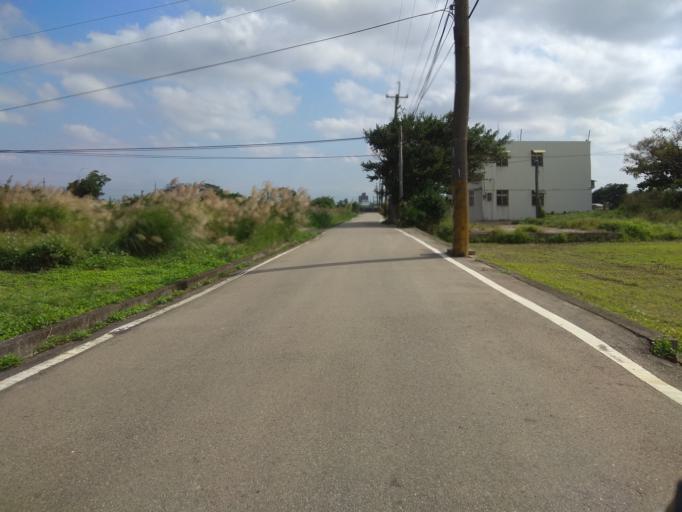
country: TW
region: Taiwan
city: Taoyuan City
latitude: 25.0614
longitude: 121.2179
